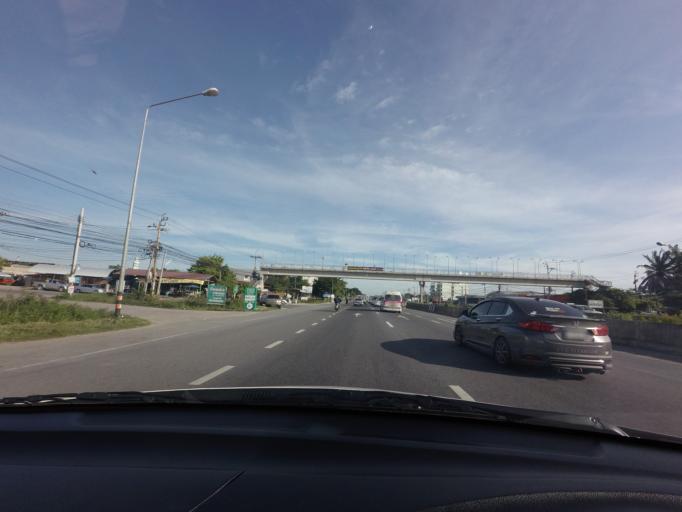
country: TH
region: Nonthaburi
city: Bang Bua Thong
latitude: 13.9522
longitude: 100.4091
